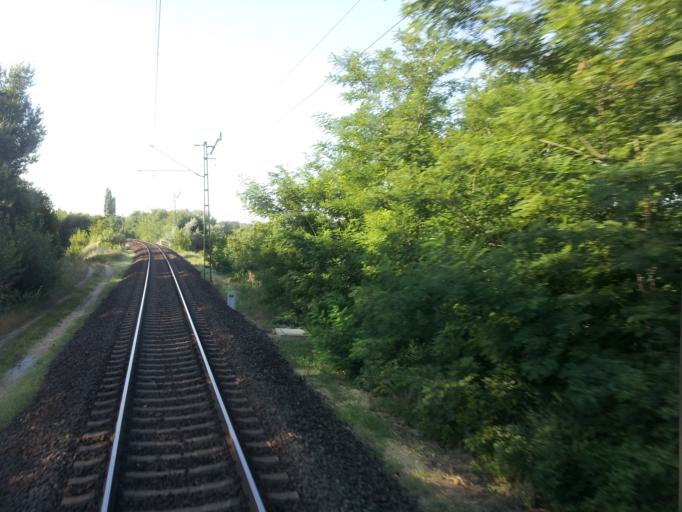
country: HU
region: Budapest
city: Budapest XX. keruelet
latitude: 47.4195
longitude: 19.1059
